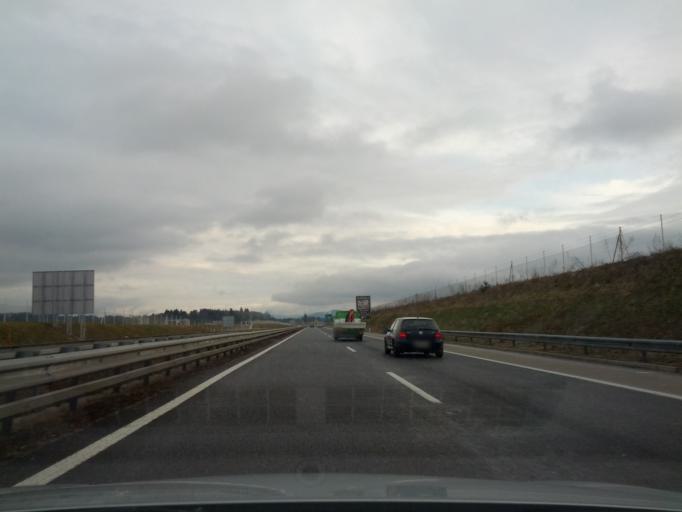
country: SI
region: Radovljica
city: Radovljica
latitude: 46.3544
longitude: 14.1740
